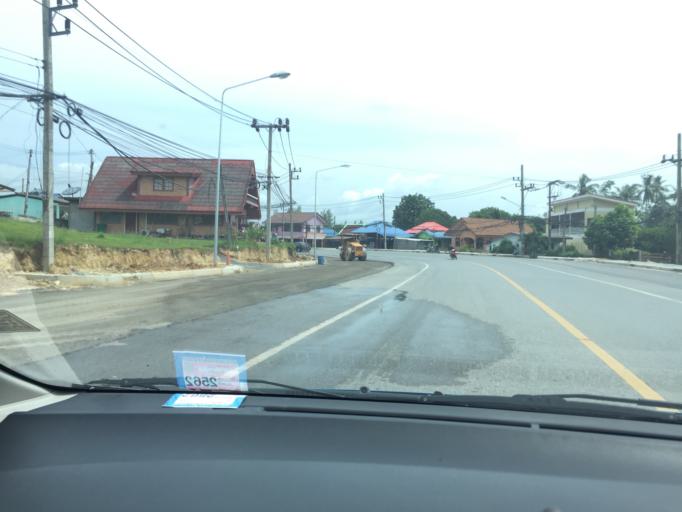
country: TH
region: Phuket
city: Mueang Phuket
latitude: 7.8331
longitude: 98.4001
